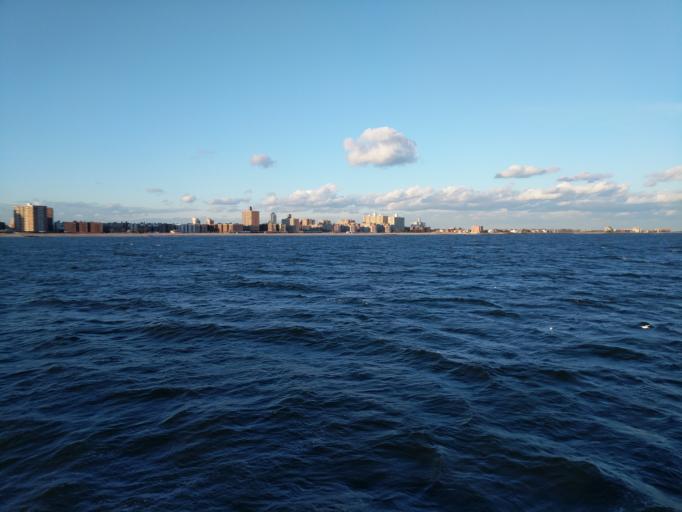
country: US
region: New York
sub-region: Kings County
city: Coney Island
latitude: 40.5658
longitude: -73.9685
